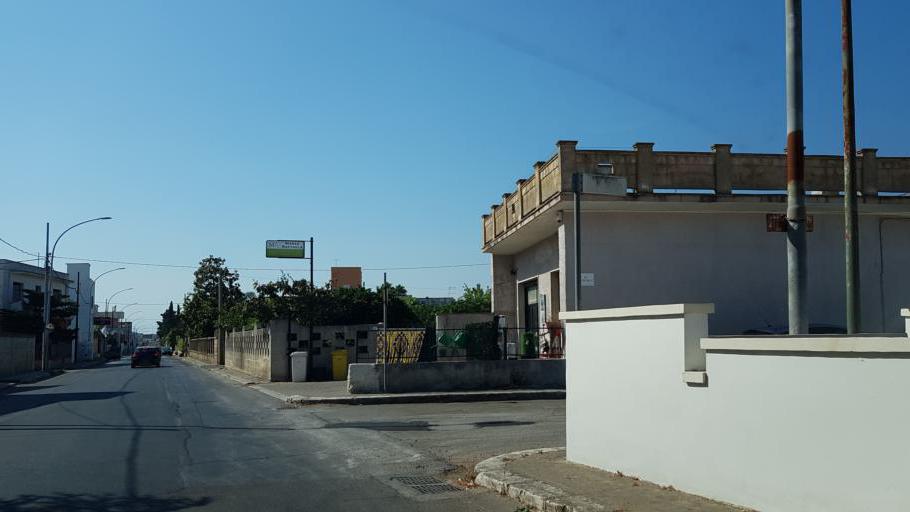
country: IT
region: Apulia
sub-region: Provincia di Brindisi
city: San Donaci
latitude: 40.4539
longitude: 17.9167
